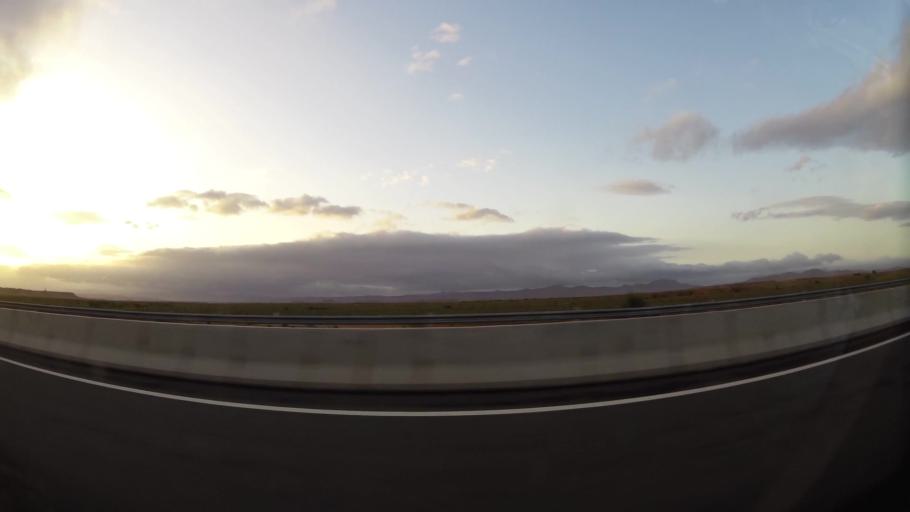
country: MA
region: Oriental
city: Taourirt
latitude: 34.5498
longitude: -2.8733
